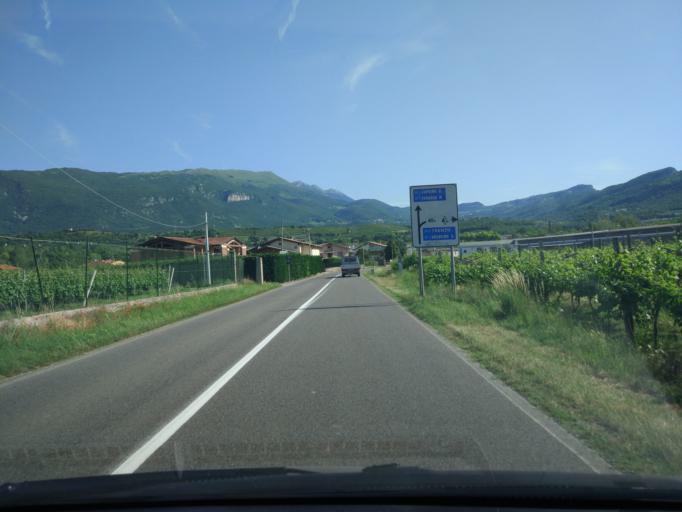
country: IT
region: Veneto
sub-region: Provincia di Verona
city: Rivoli Veronese
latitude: 45.5816
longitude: 10.8082
